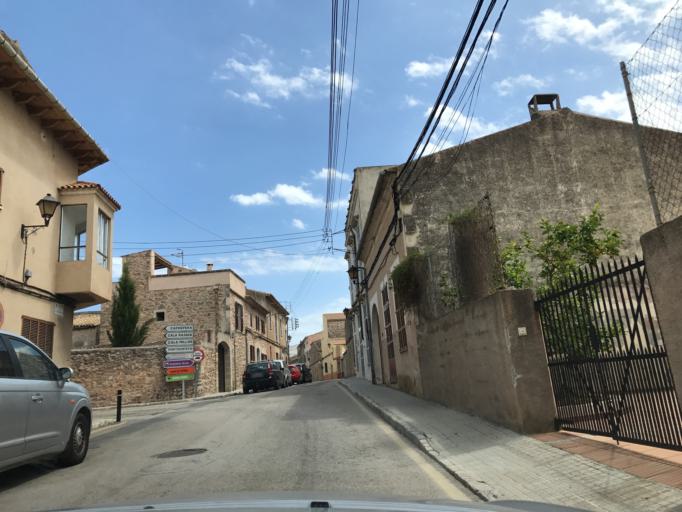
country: ES
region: Balearic Islands
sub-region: Illes Balears
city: Son Servera
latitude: 39.6235
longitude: 3.3576
